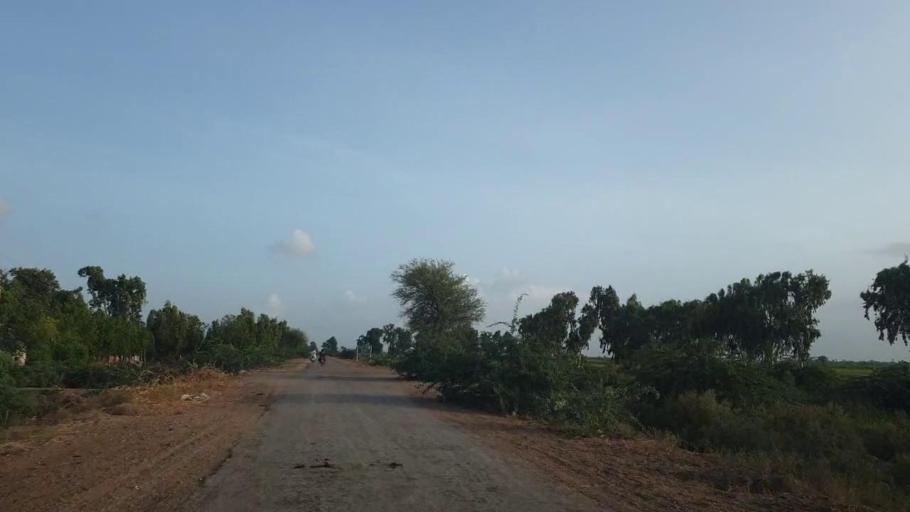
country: PK
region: Sindh
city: Kadhan
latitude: 24.6166
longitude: 69.1158
